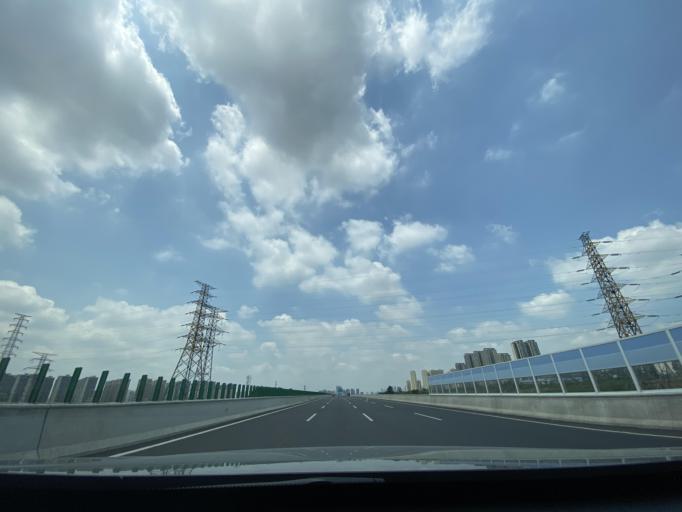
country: CN
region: Sichuan
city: Chengdu
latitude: 30.5901
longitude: 104.1245
